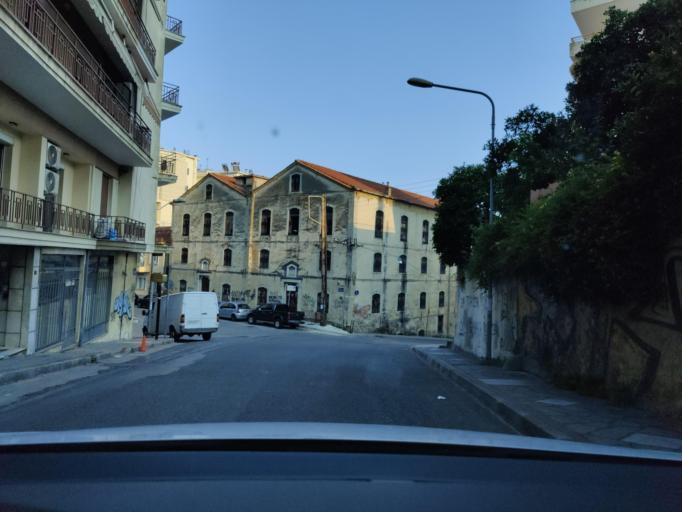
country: GR
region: East Macedonia and Thrace
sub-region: Nomos Kavalas
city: Kavala
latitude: 40.9384
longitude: 24.4059
